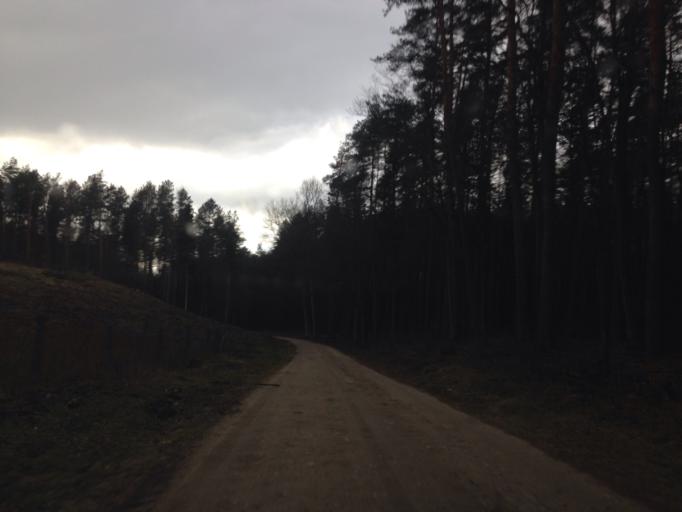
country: PL
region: Kujawsko-Pomorskie
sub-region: Powiat brodnicki
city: Gorzno
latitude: 53.1849
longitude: 19.6728
